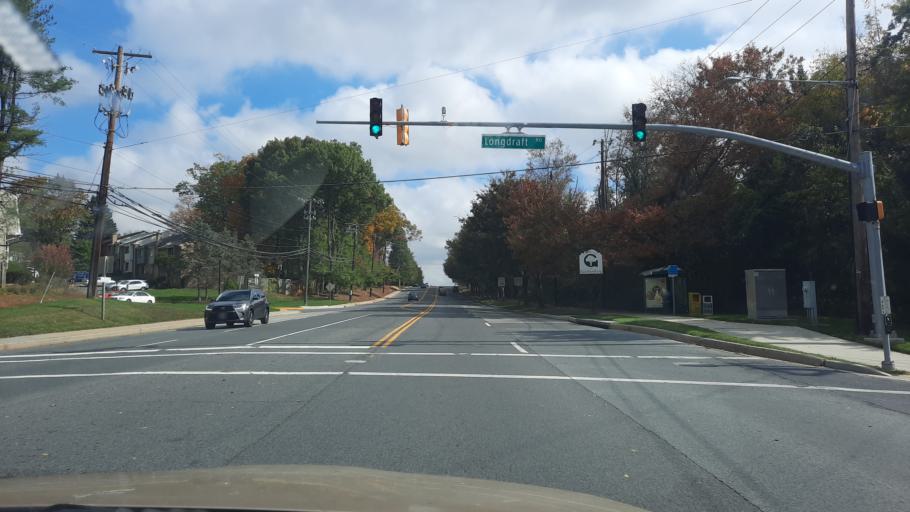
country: US
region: Maryland
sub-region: Montgomery County
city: Gaithersburg
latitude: 39.1483
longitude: -77.2379
